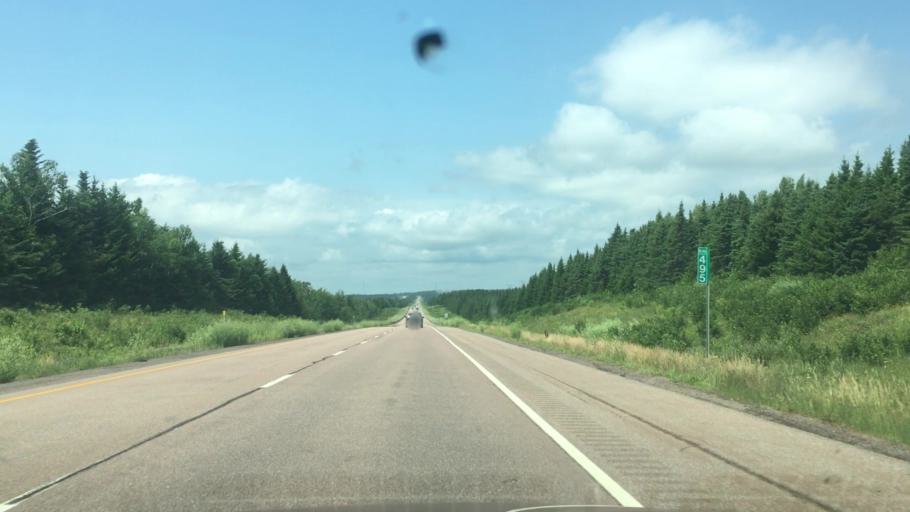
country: CA
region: New Brunswick
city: Sackville
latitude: 45.9720
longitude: -64.4384
